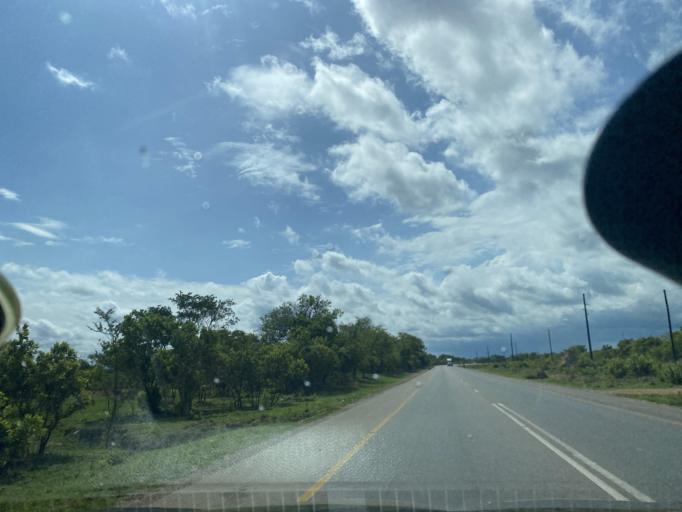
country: ZM
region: Lusaka
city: Kafue
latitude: -15.8584
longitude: 28.2640
